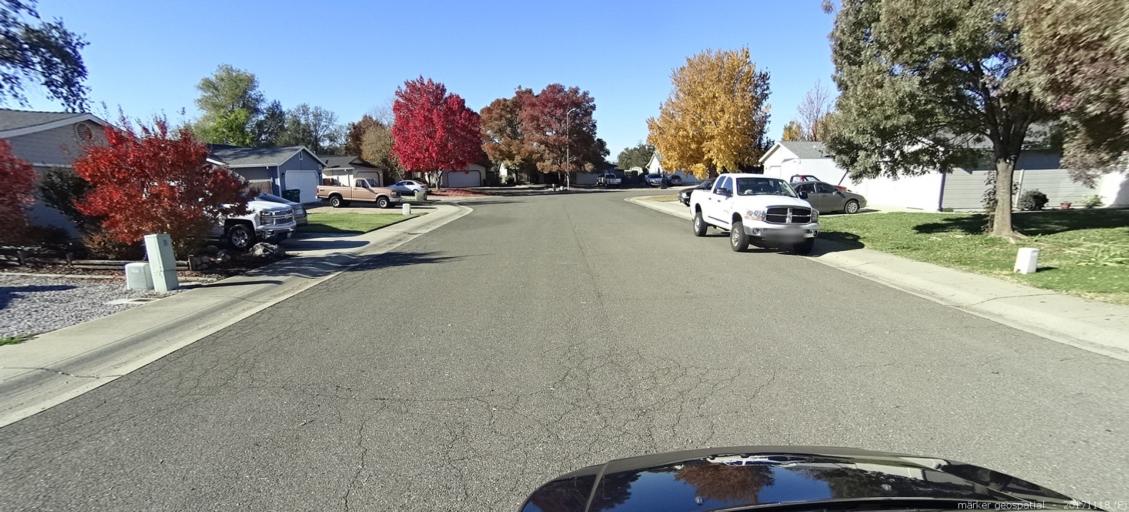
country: US
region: California
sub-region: Shasta County
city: Cottonwood
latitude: 40.3898
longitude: -122.2776
